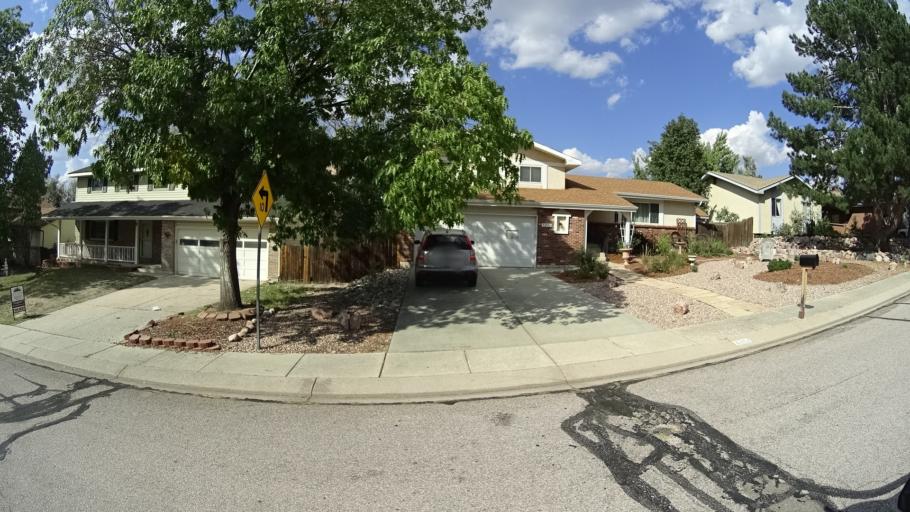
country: US
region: Colorado
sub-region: El Paso County
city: Cimarron Hills
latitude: 38.8748
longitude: -104.7315
